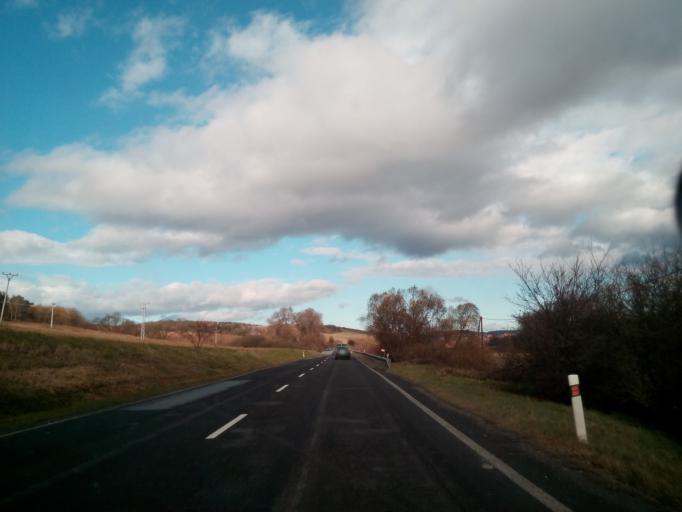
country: SK
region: Presovsky
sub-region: Okres Bardejov
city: Bardejov
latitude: 49.1662
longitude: 21.3111
